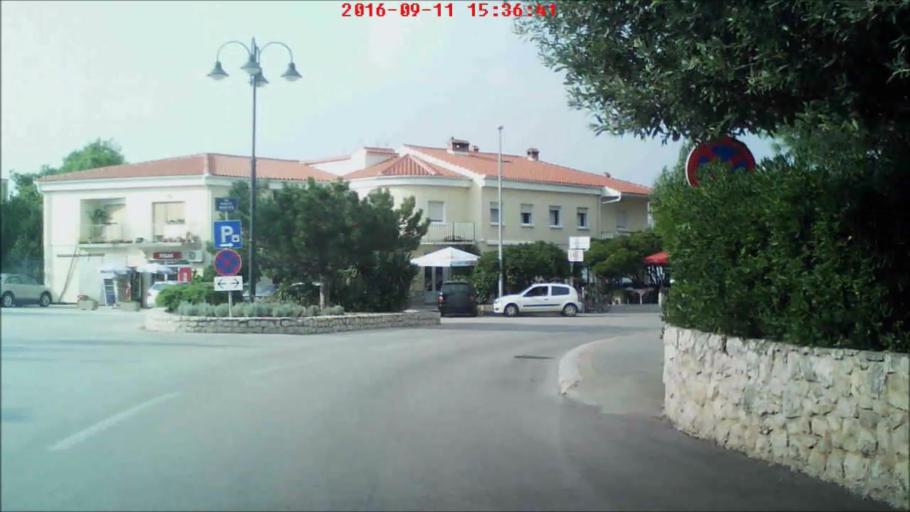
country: HR
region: Zadarska
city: Nin
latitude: 44.2404
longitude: 15.1807
